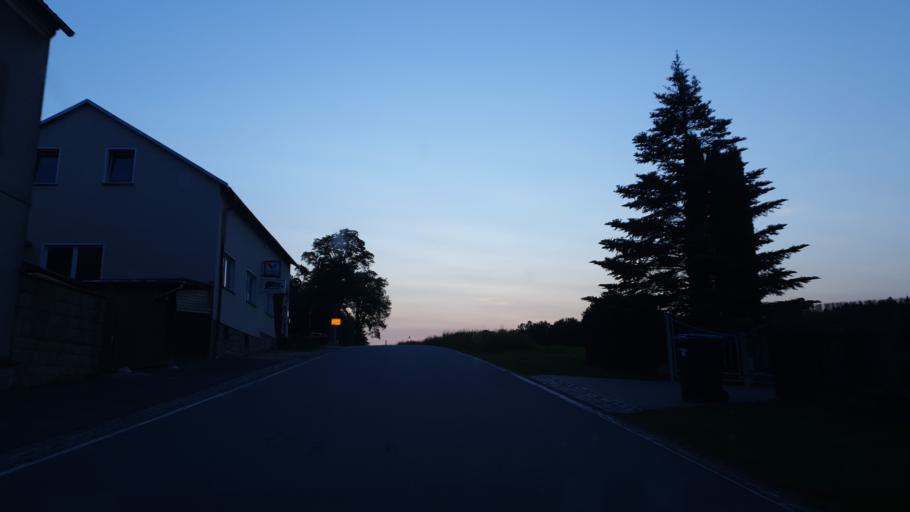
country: DE
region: Saxony
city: Zschorlau
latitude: 50.5535
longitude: 12.6583
